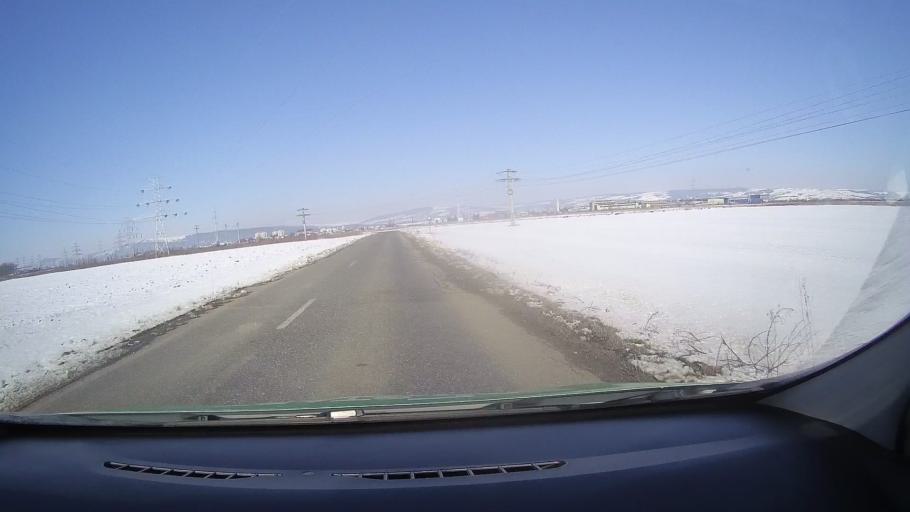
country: RO
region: Brasov
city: Fogarasch
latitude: 45.8163
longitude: 24.9874
